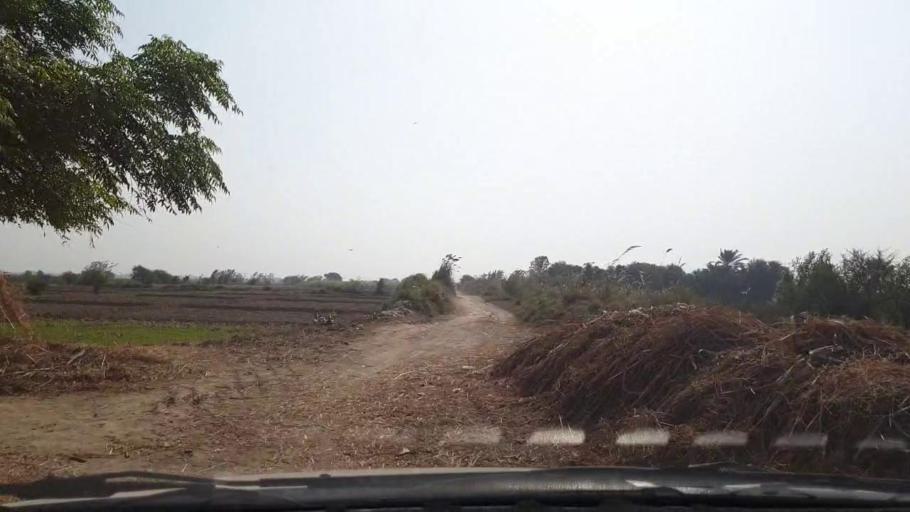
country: PK
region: Sindh
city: Tando Muhammad Khan
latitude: 25.0871
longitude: 68.3585
